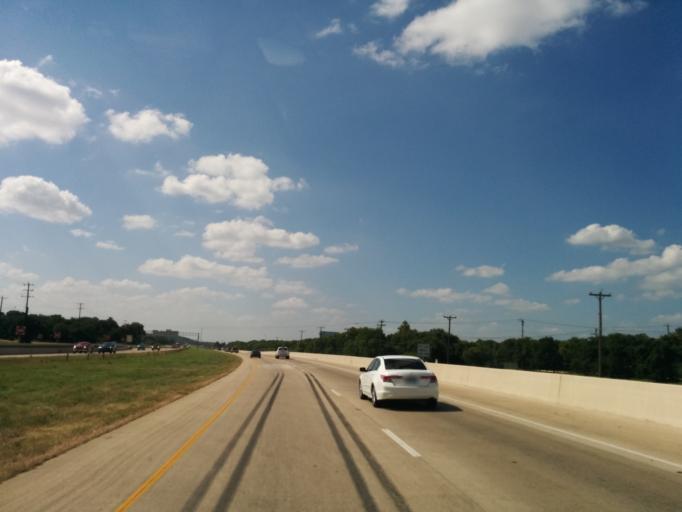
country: US
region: Texas
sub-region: Bexar County
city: Cross Mountain
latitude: 29.6350
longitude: -98.6135
